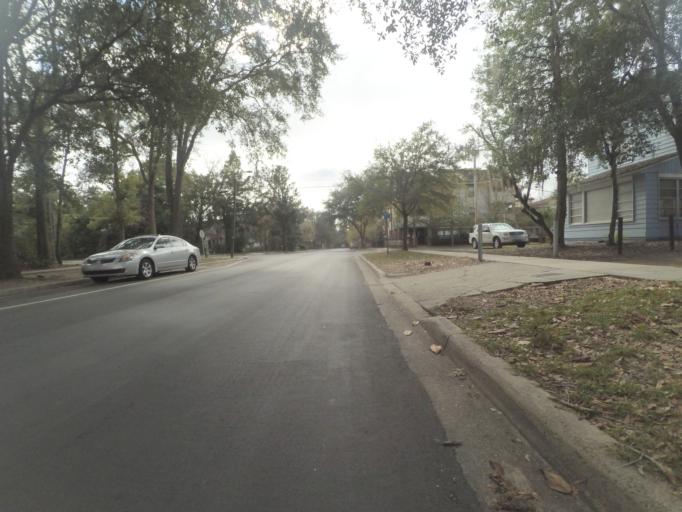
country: US
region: Florida
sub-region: Alachua County
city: Gainesville
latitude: 29.6471
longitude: -82.3351
